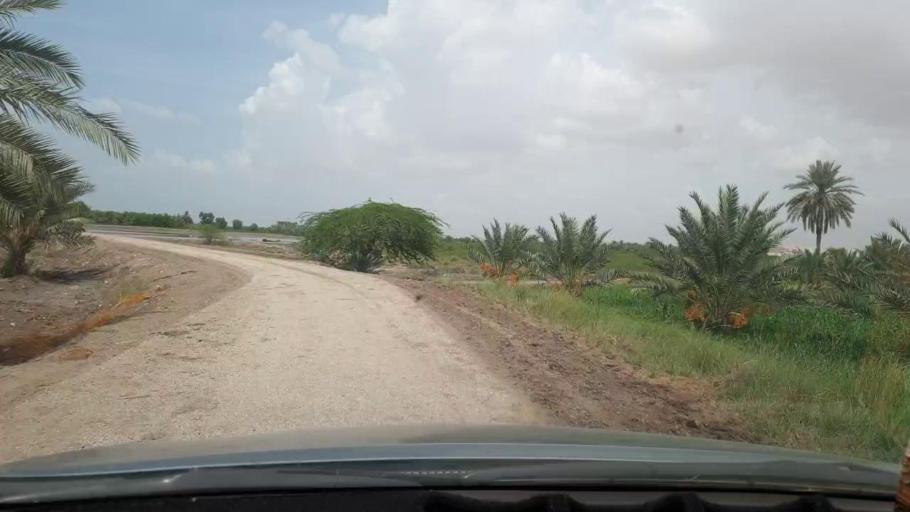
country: PK
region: Sindh
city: Khairpur
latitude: 27.4550
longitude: 68.8250
